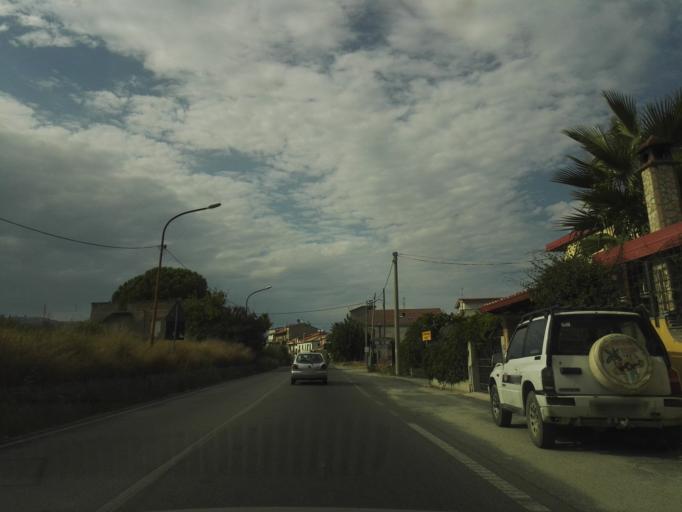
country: IT
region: Calabria
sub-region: Provincia di Catanzaro
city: Marina di Davoli
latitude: 38.6582
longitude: 16.5464
